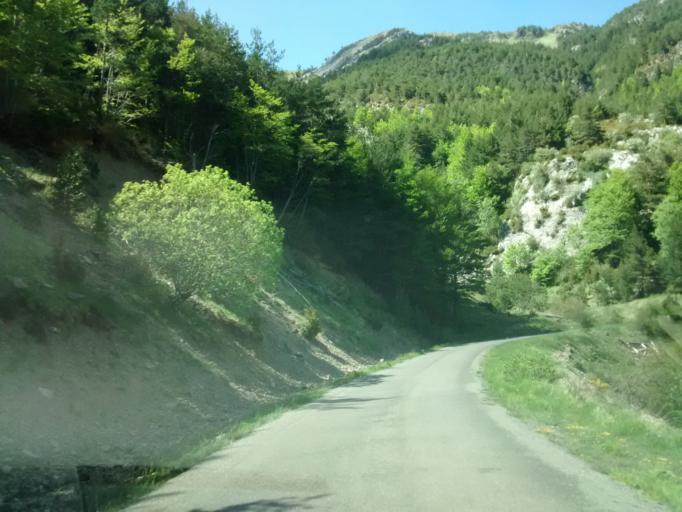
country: ES
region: Aragon
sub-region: Provincia de Huesca
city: Canfranc
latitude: 42.7357
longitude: -0.5942
